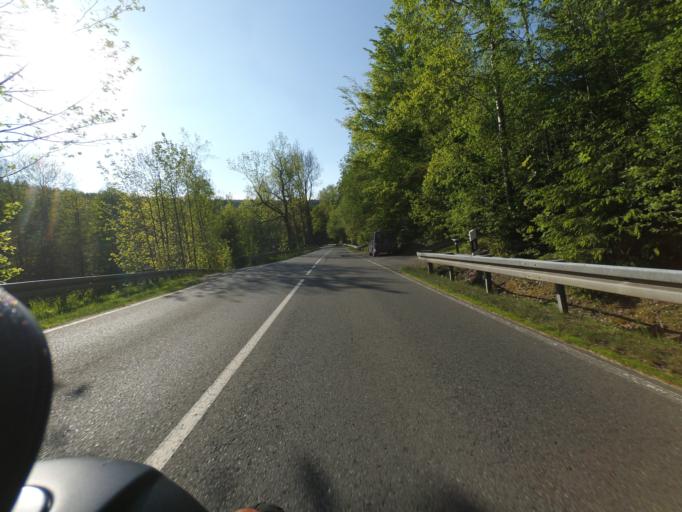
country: DE
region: Saxony
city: Obercunnersdorf
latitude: 50.8774
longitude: 13.5710
